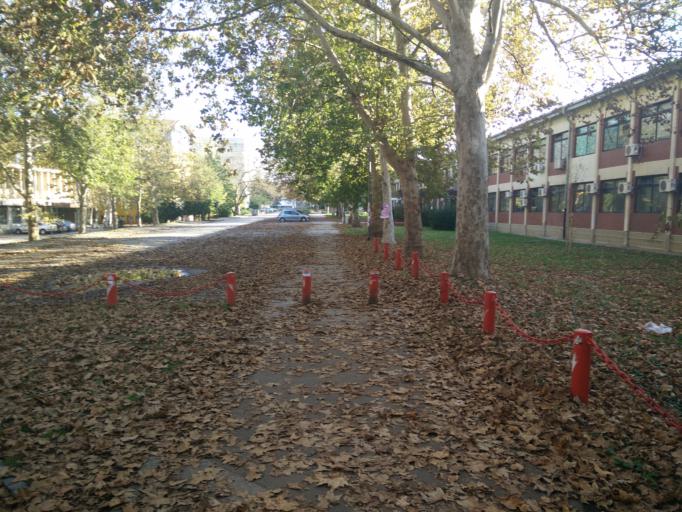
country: RS
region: Autonomna Pokrajina Vojvodina
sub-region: Juznobacki Okrug
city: Novi Sad
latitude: 45.2464
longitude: 19.8506
